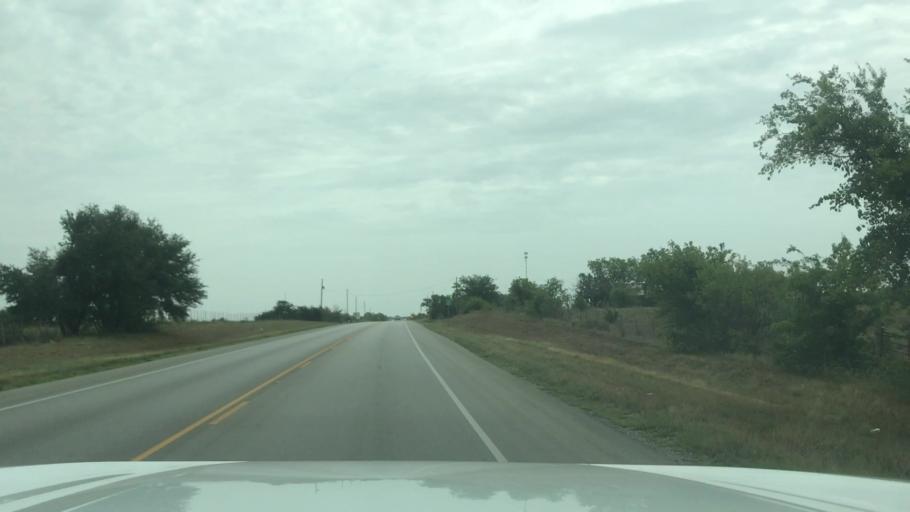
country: US
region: Texas
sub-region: Erath County
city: Dublin
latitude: 32.0969
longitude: -98.3800
